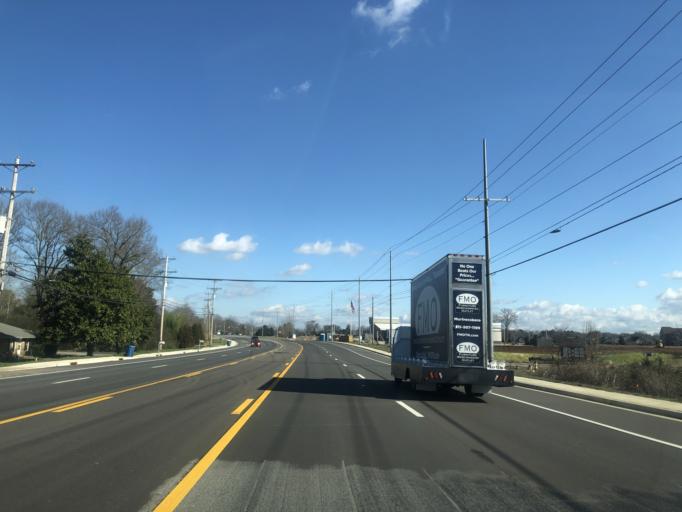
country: US
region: Tennessee
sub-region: Rutherford County
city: Murfreesboro
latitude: 35.8429
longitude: -86.4891
